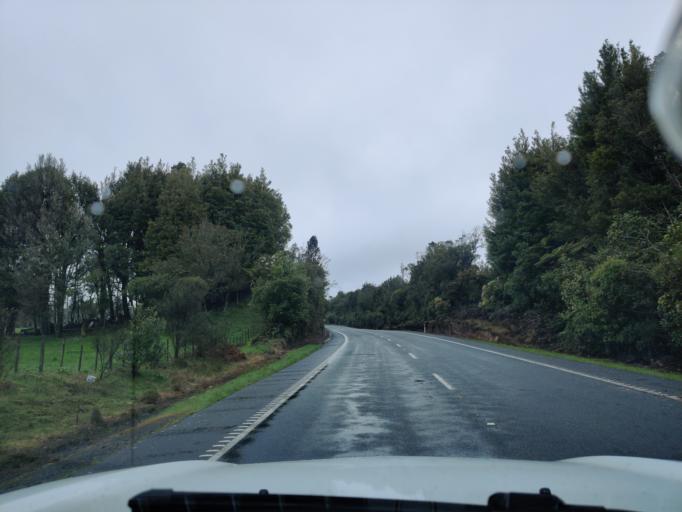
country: NZ
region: Bay of Plenty
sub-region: Rotorua District
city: Rotorua
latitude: -38.0591
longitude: 176.0923
